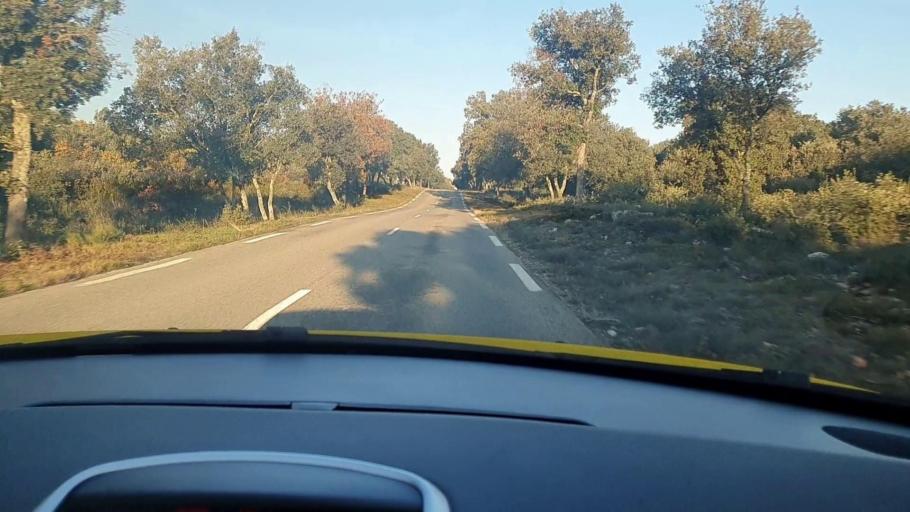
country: FR
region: Languedoc-Roussillon
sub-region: Departement du Gard
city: Montaren-et-Saint-Mediers
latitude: 44.1076
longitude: 4.3779
